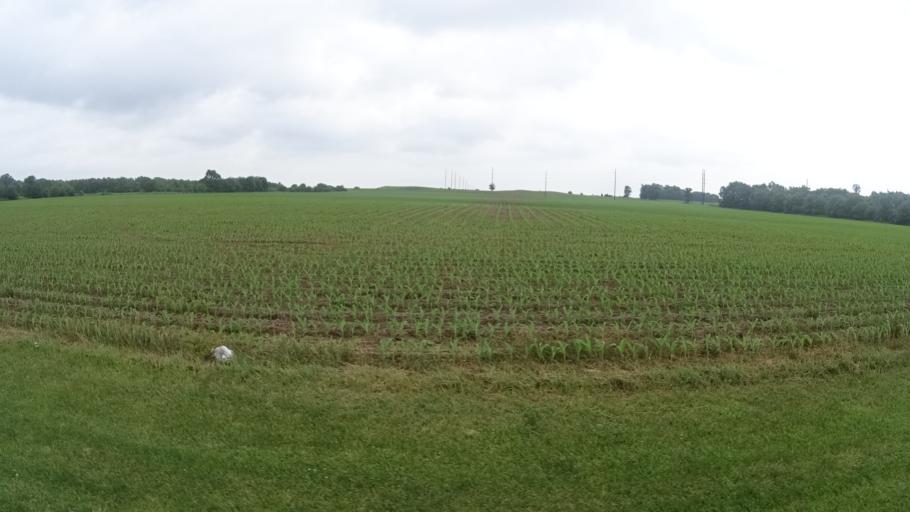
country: US
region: Ohio
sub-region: Huron County
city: Bellevue
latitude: 41.3538
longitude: -82.7730
